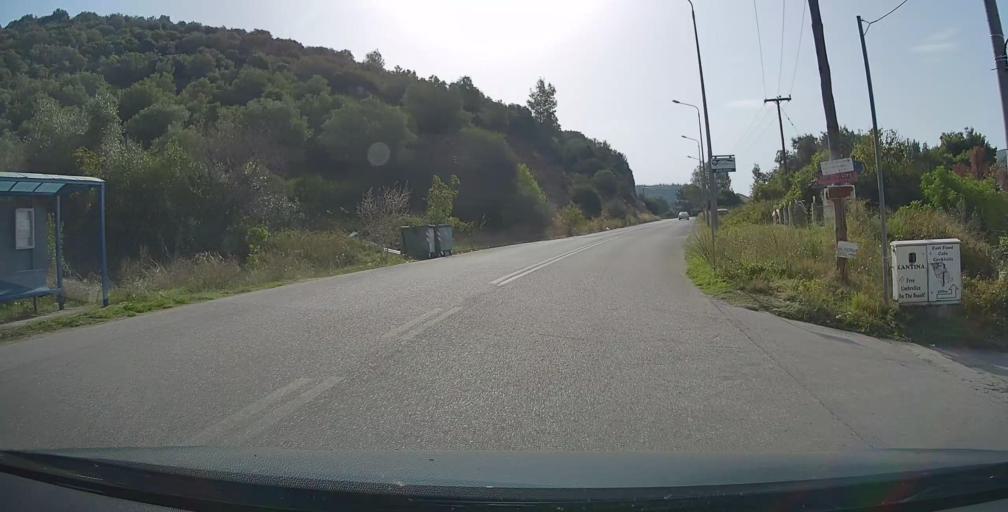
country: GR
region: Central Macedonia
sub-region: Nomos Chalkidikis
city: Sykia
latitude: 39.9717
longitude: 23.9187
